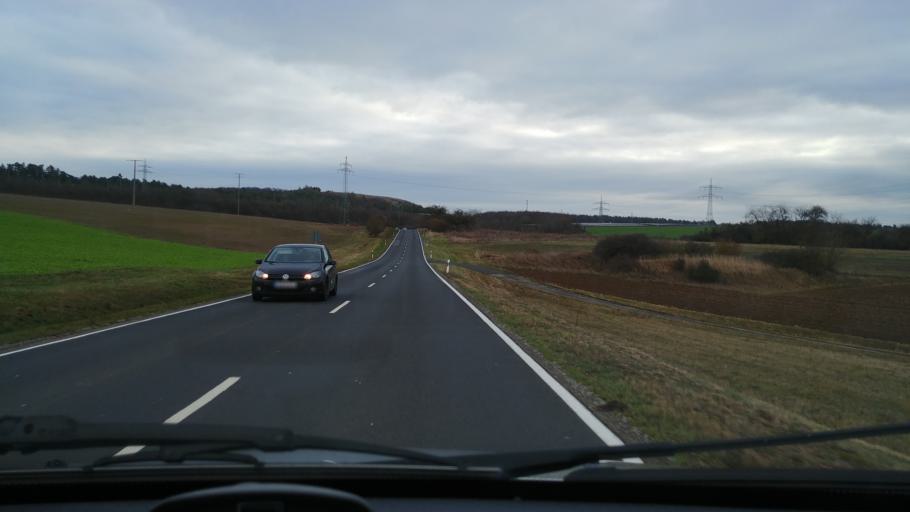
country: DE
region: Bavaria
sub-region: Regierungsbezirk Unterfranken
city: Steinfeld
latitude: 49.9884
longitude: 9.6920
